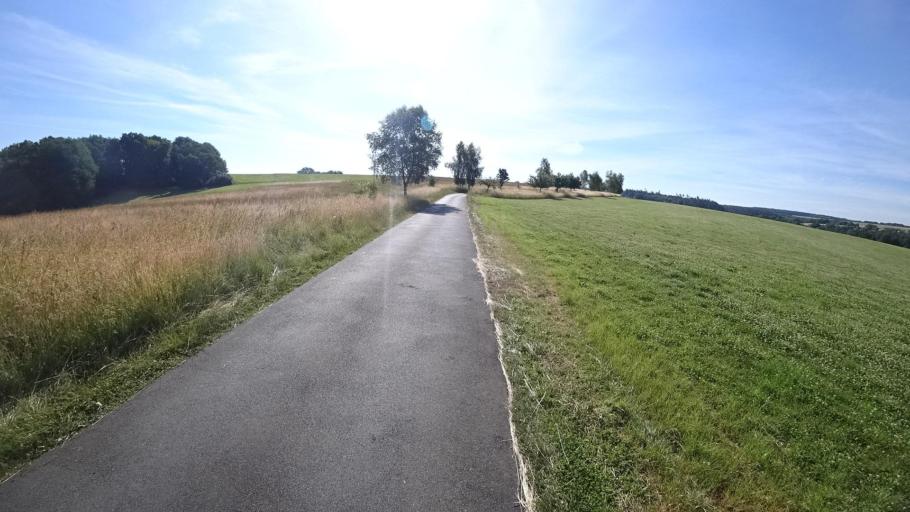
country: DE
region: Rheinland-Pfalz
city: Oberwambach
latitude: 50.6774
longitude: 7.6604
